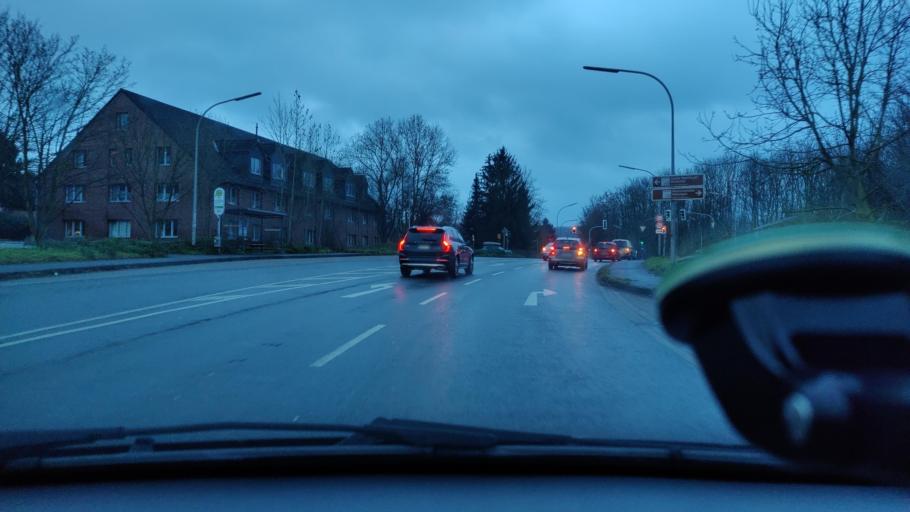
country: DE
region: North Rhine-Westphalia
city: Witten
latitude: 51.4288
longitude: 7.2919
